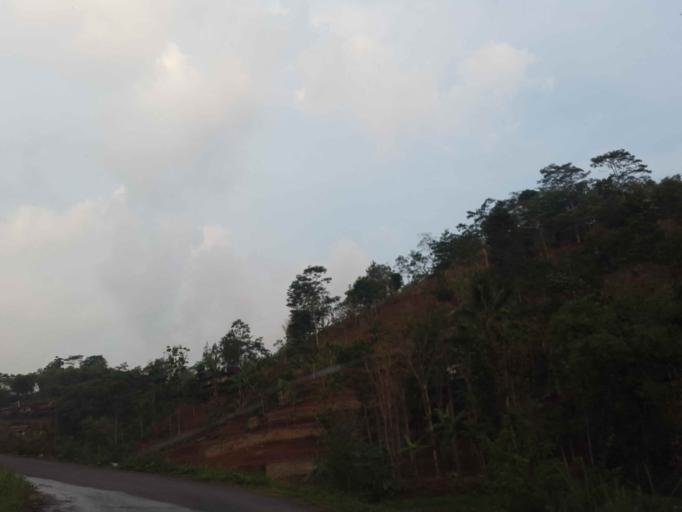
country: ID
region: Central Java
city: Jatiroto
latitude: -7.7397
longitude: 111.1128
